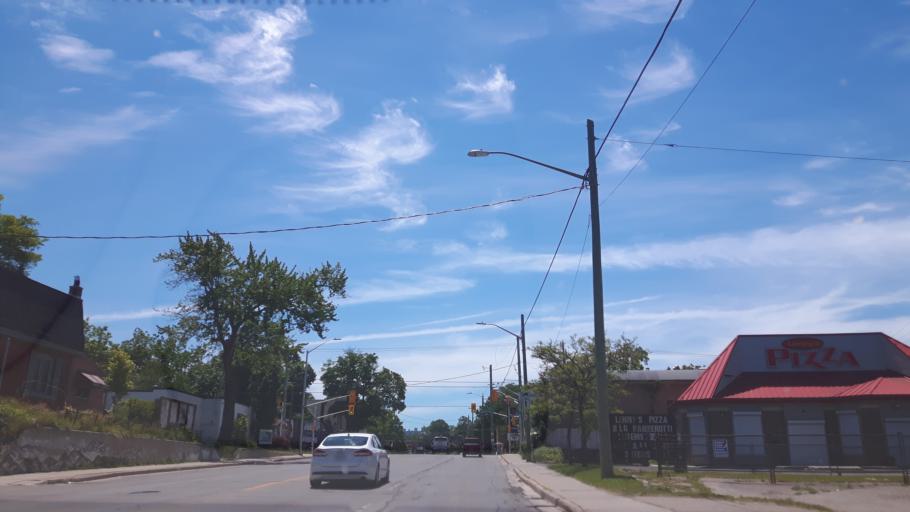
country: CA
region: Ontario
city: London
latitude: 42.9732
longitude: -81.2390
